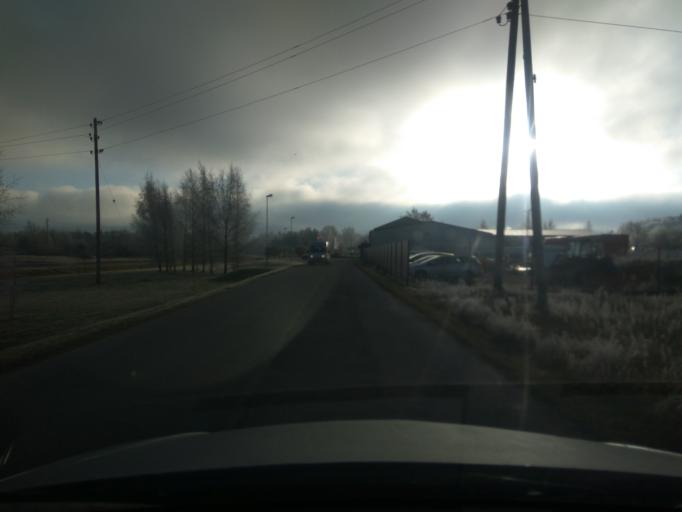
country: LV
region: Kuldigas Rajons
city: Kuldiga
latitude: 56.9672
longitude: 21.9339
